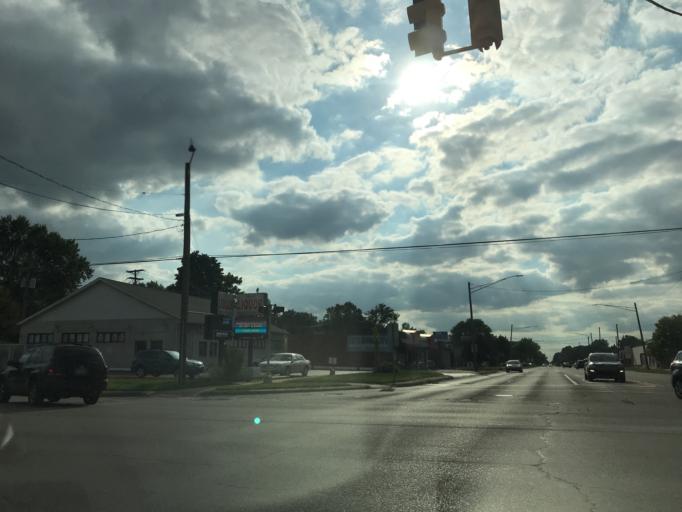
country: US
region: Michigan
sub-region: Wayne County
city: Redford
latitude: 42.4140
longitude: -83.2963
